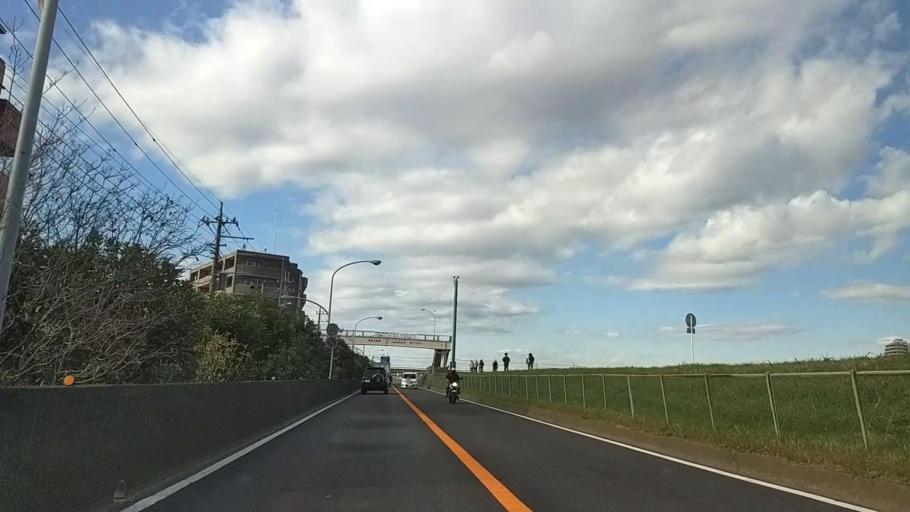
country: JP
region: Tokyo
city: Chofugaoka
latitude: 35.6054
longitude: 139.6277
